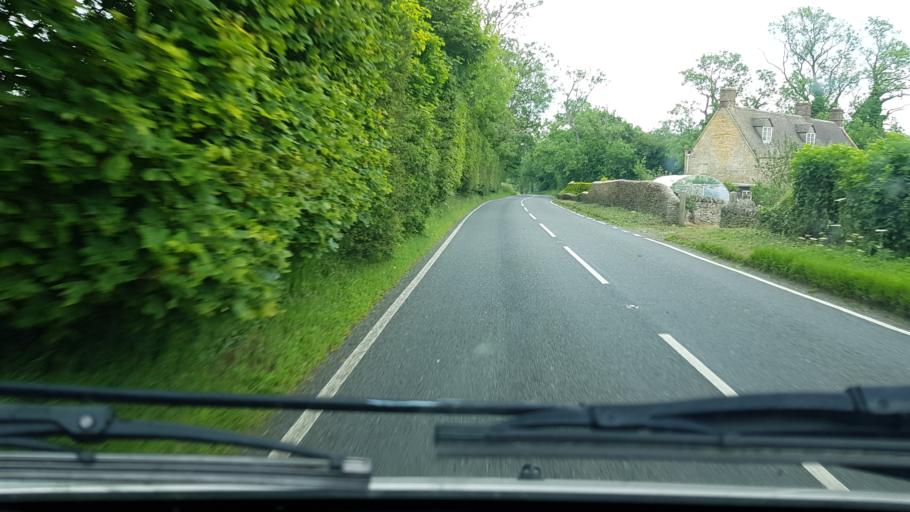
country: GB
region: England
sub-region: Gloucestershire
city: Donnington
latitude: 51.9506
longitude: -1.7405
